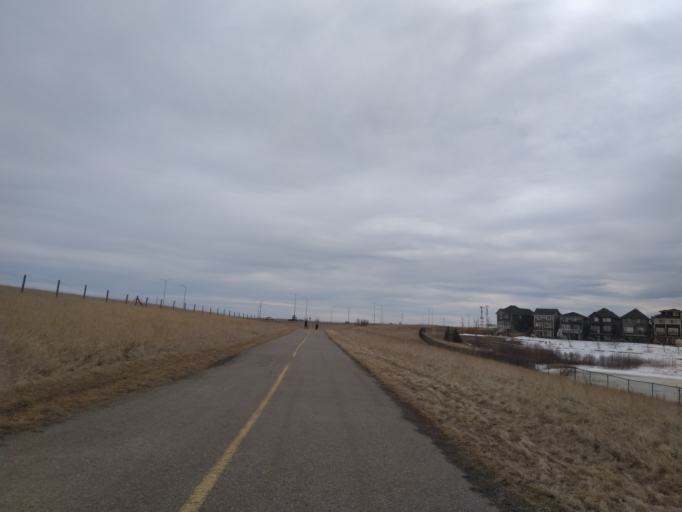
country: CA
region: Alberta
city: Chestermere
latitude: 51.1343
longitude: -113.9247
